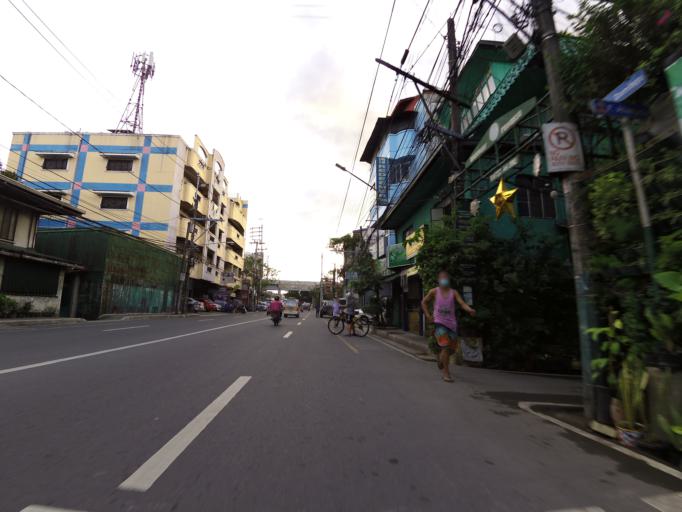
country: PH
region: Metro Manila
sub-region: San Juan
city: San Juan
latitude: 14.6027
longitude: 121.0210
